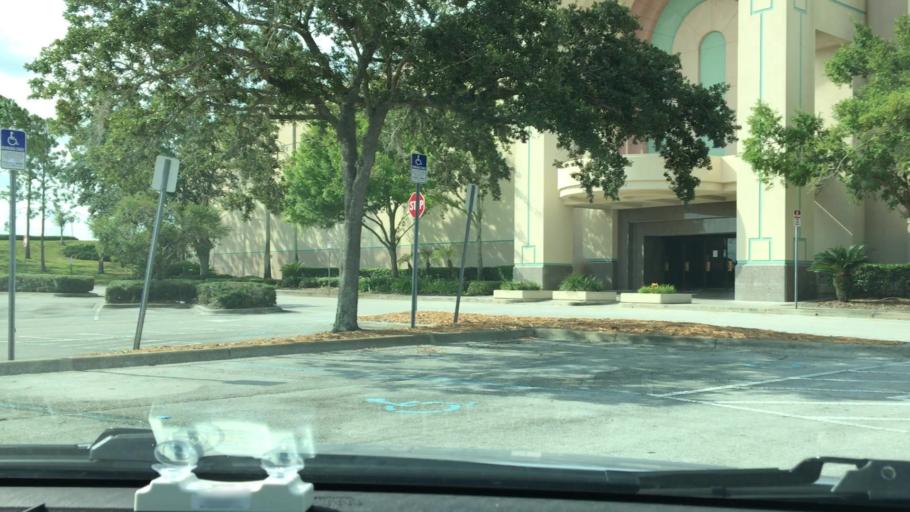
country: US
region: Florida
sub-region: Seminole County
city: Lake Mary
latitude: 28.8063
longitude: -81.3375
